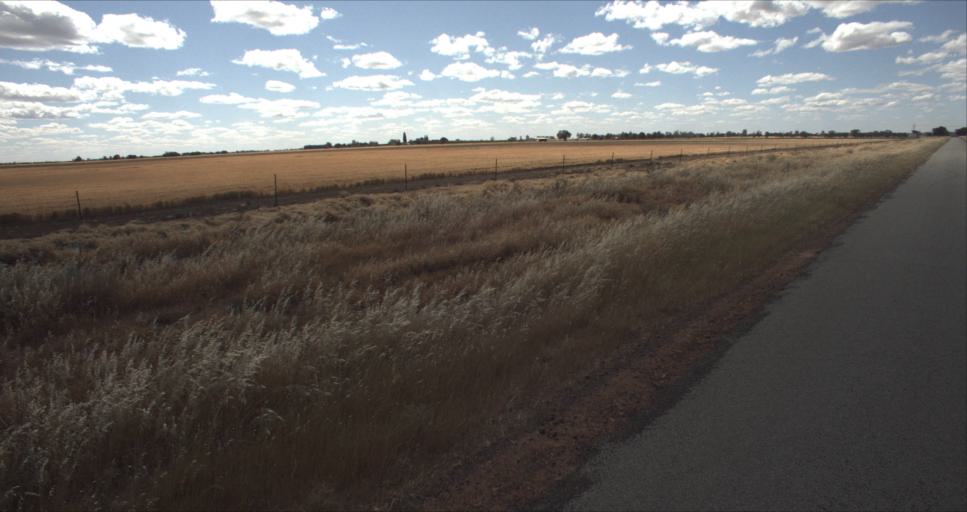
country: AU
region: New South Wales
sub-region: Leeton
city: Leeton
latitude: -34.5023
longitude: 146.2452
